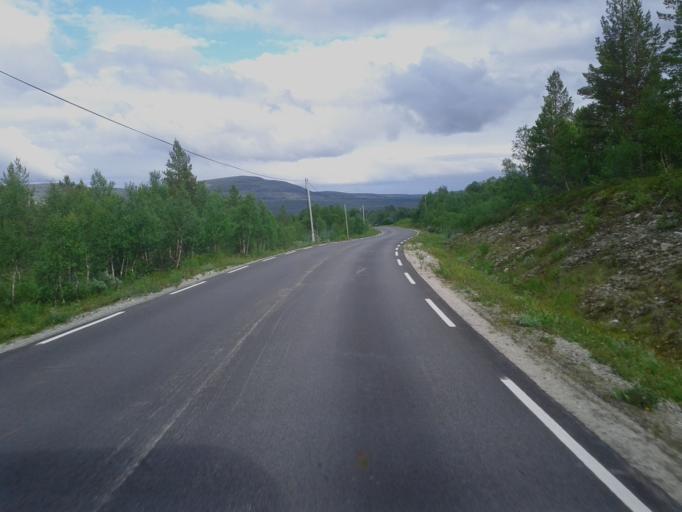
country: NO
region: Sor-Trondelag
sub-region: Roros
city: Roros
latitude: 62.3075
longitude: 11.6898
